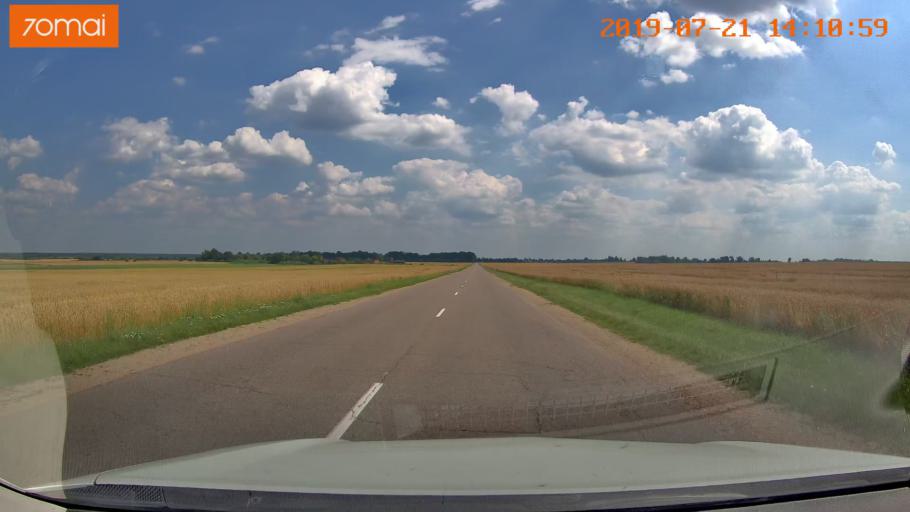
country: BY
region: Grodnenskaya
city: Karelichy
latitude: 53.6608
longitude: 26.1426
